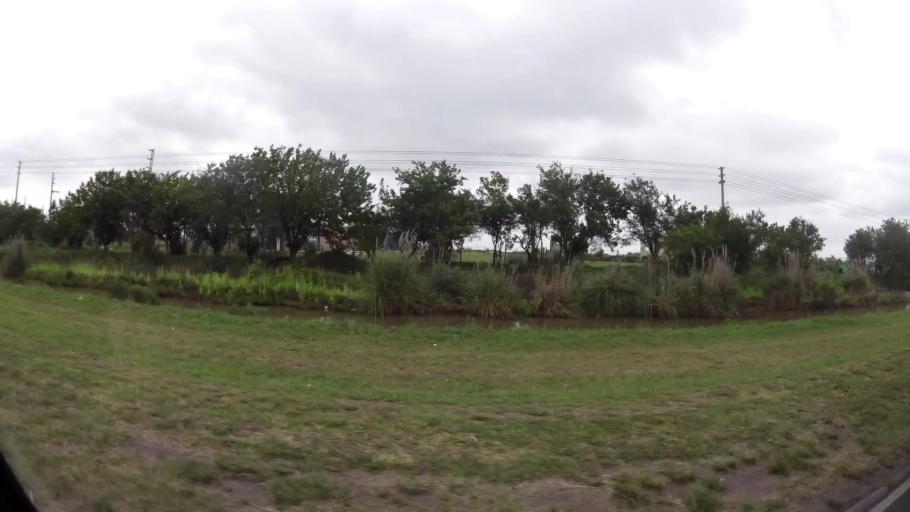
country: AR
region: Buenos Aires
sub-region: Partido de San Vicente
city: San Vicente
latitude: -34.9600
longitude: -58.4651
